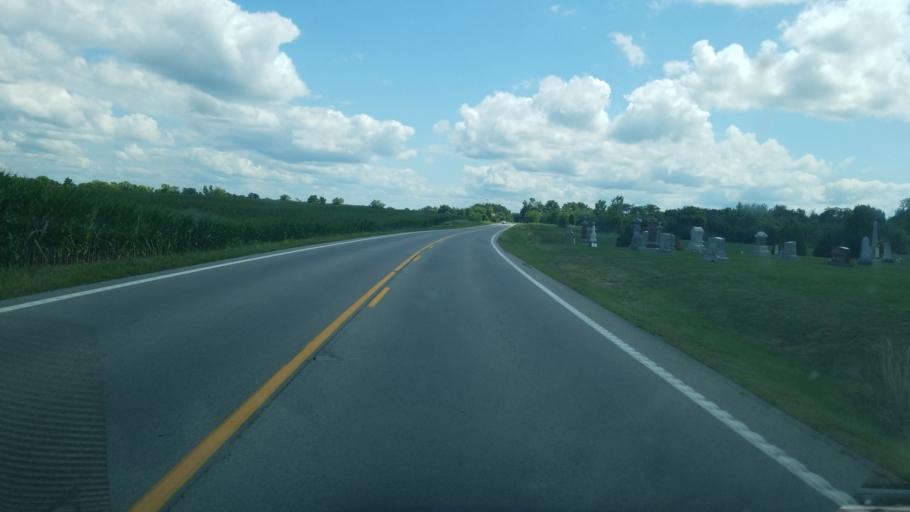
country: US
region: Ohio
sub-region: Putnam County
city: Kalida
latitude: 40.9465
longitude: -84.1621
